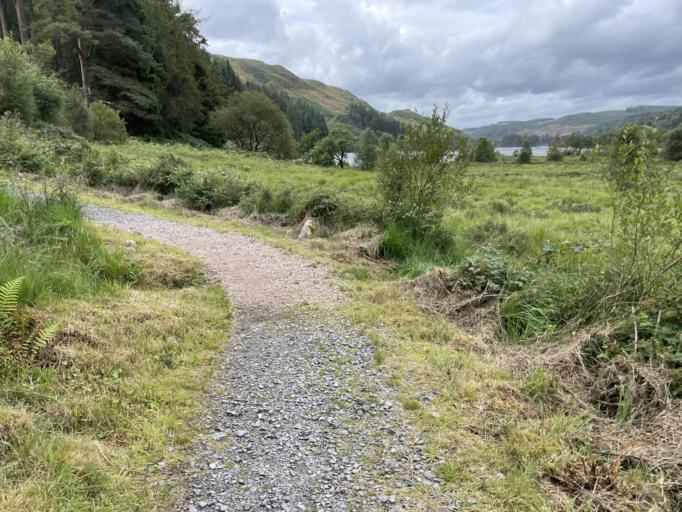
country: GB
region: Scotland
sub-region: Dumfries and Galloway
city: Newton Stewart
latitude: 55.0897
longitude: -4.4703
